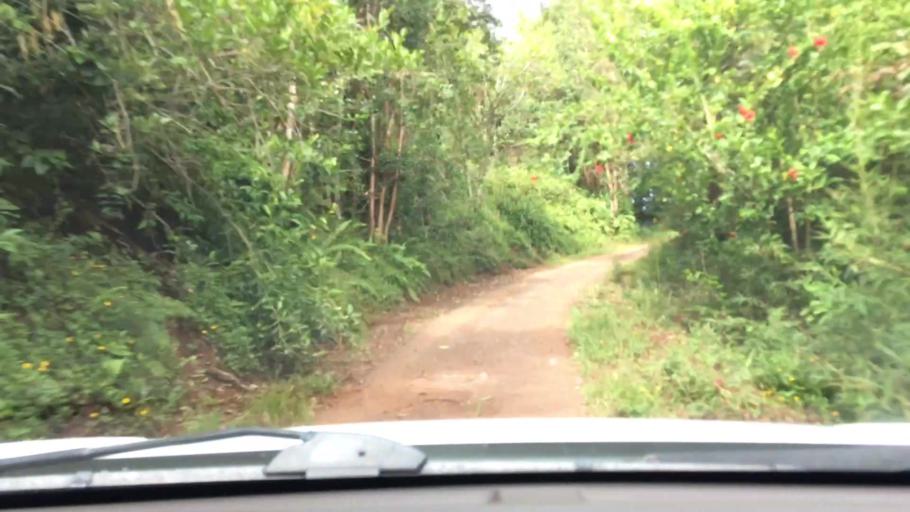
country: US
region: Hawaii
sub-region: Hawaii County
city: Pepeekeo
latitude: 19.8262
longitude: -155.1122
